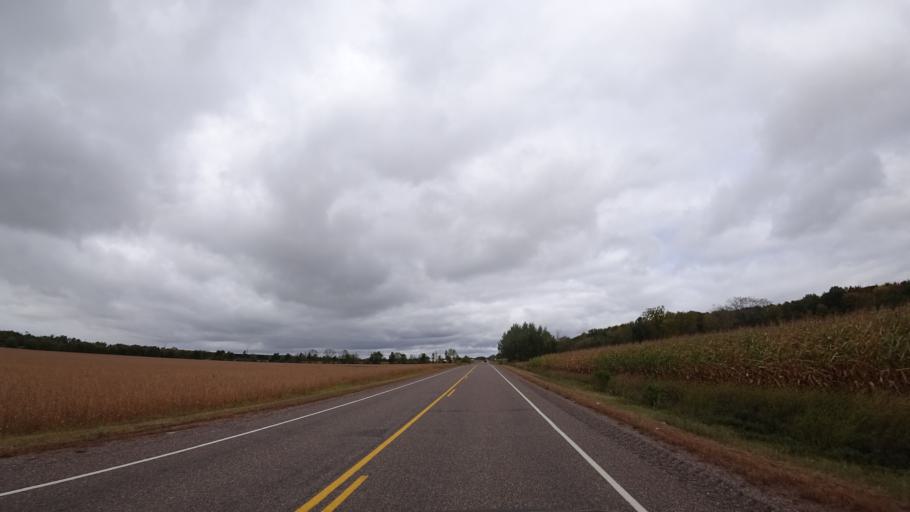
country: US
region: Wisconsin
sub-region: Chippewa County
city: Lake Wissota
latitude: 44.9980
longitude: -91.2867
